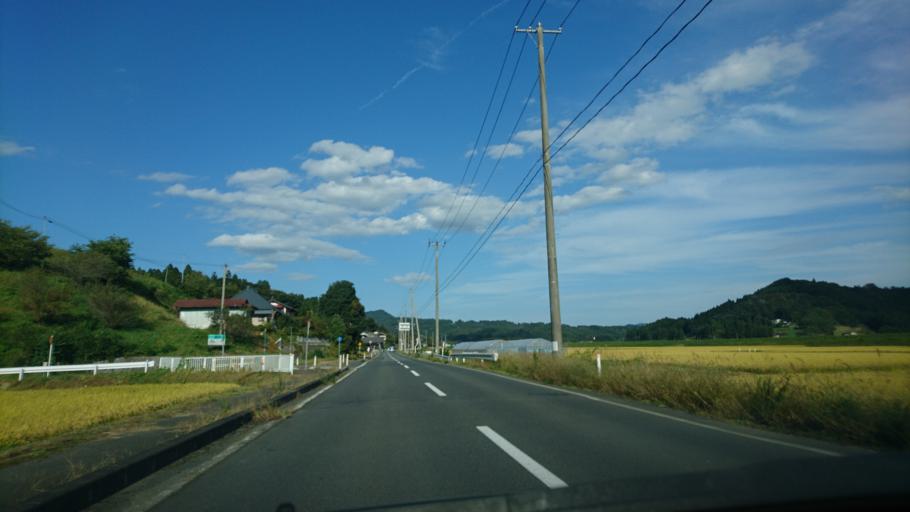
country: JP
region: Iwate
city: Ichinoseki
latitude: 38.8458
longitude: 141.2688
